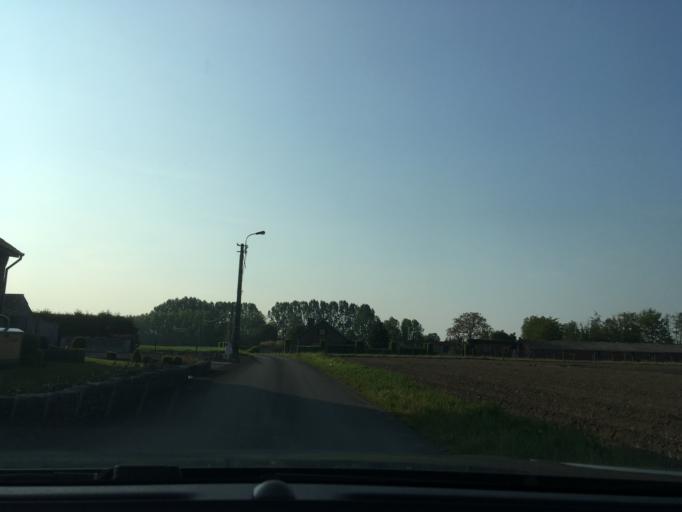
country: BE
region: Flanders
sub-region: Provincie West-Vlaanderen
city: Lichtervelde
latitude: 51.0217
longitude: 3.1596
